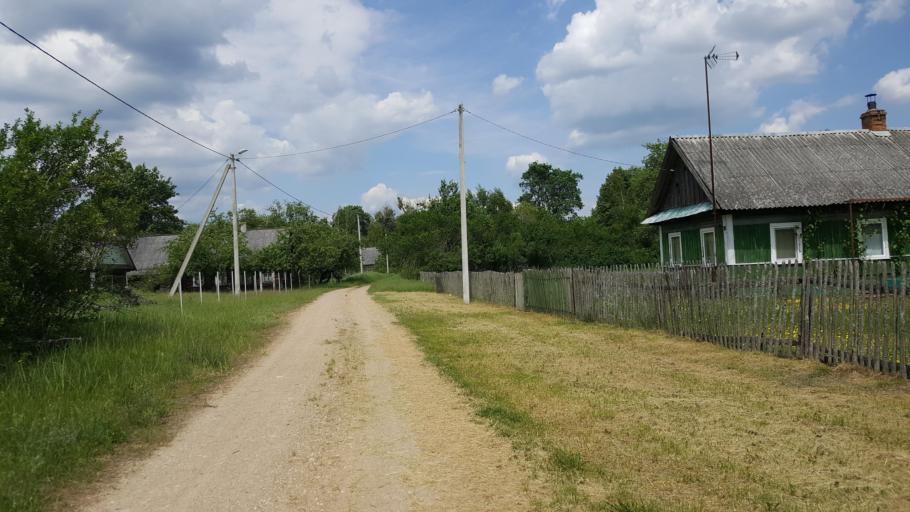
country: PL
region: Podlasie
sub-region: Powiat hajnowski
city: Bialowieza
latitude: 52.5755
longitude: 24.0995
